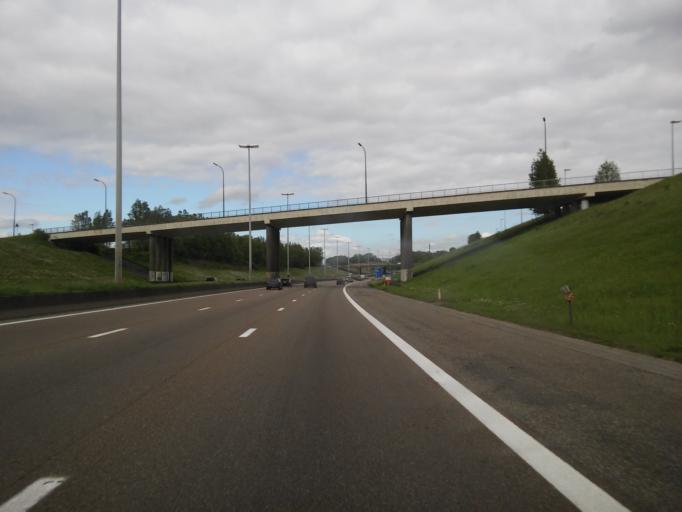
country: BE
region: Flanders
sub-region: Provincie Vlaams-Brabant
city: Bever
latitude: 50.9135
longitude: 4.3433
